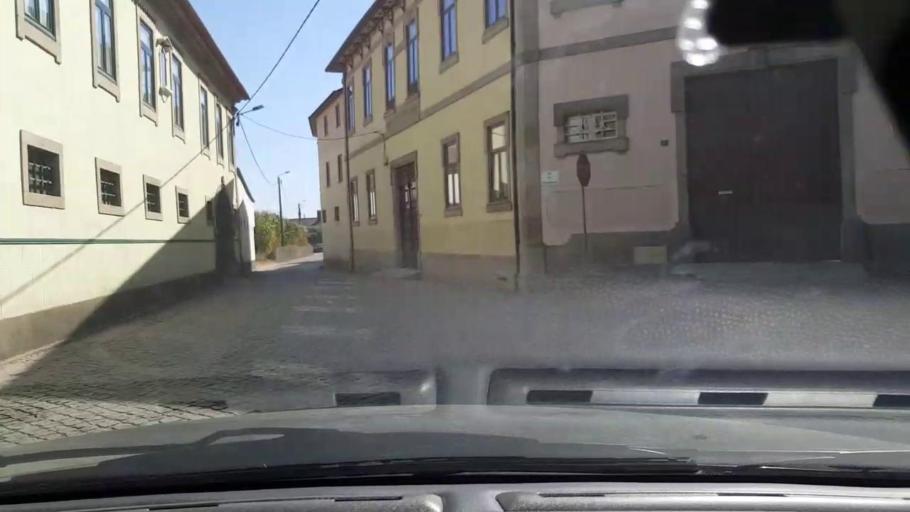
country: PT
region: Porto
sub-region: Matosinhos
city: Lavra
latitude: 41.2918
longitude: -8.6901
